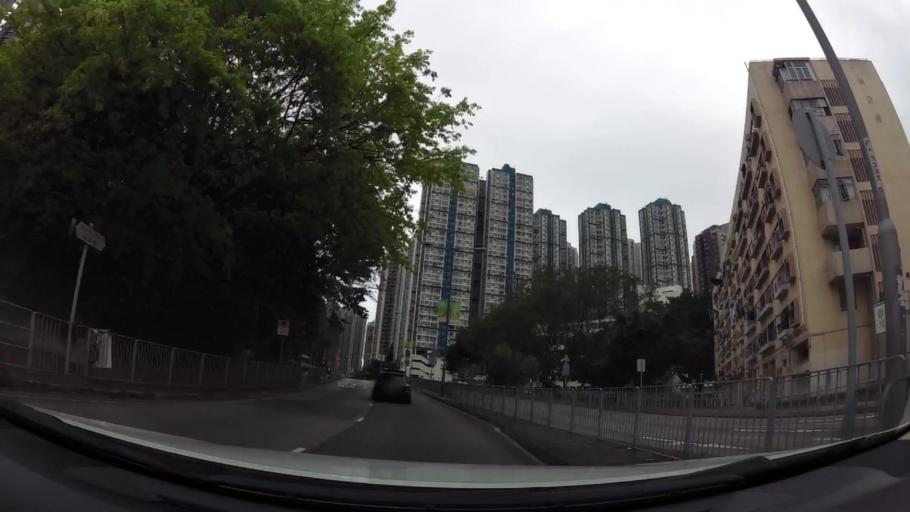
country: HK
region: Tuen Mun
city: Tuen Mun
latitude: 22.4028
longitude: 113.9729
